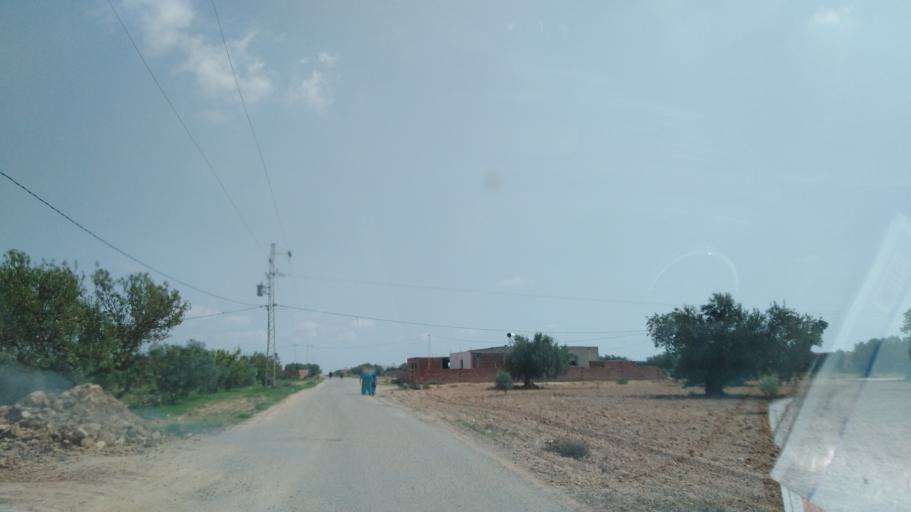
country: TN
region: Safaqis
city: Sfax
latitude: 34.6358
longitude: 10.6087
